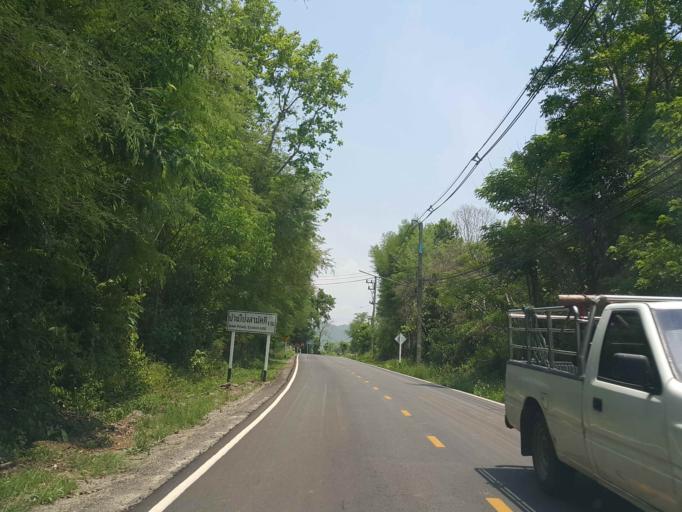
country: TH
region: Chiang Mai
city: Mae On
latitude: 18.9141
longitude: 99.2364
